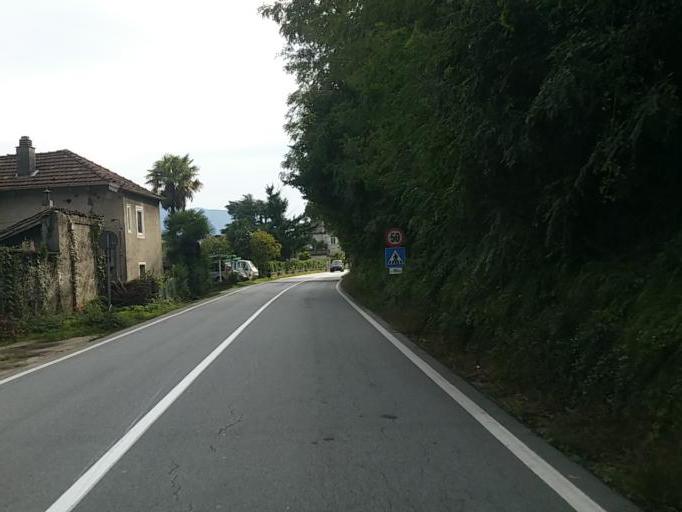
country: IT
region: Piedmont
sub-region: Provincia Verbano-Cusio-Ossola
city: Gonte
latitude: 46.0037
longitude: 8.6585
